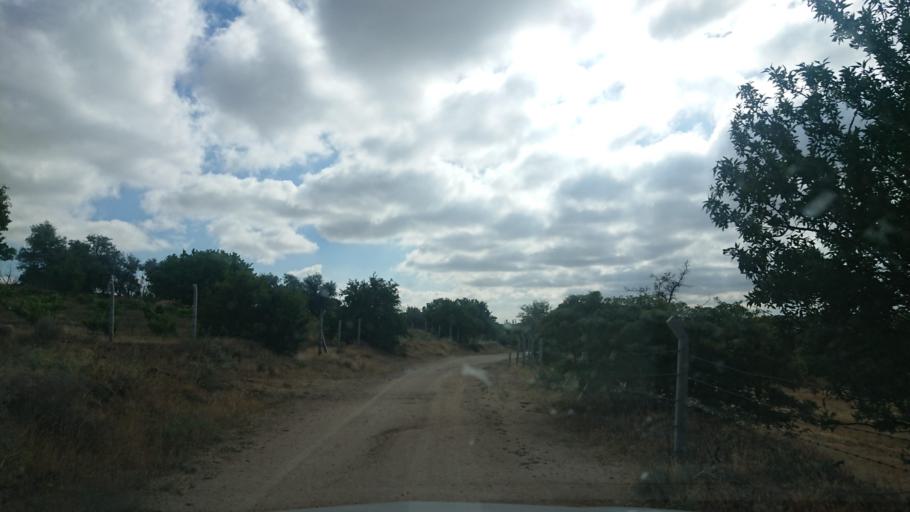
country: TR
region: Aksaray
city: Agacoren
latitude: 38.8639
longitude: 33.9444
